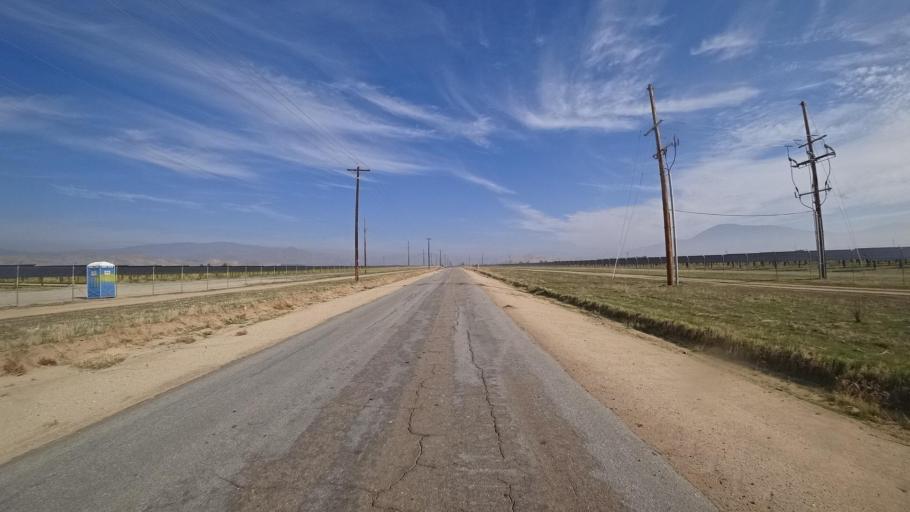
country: US
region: California
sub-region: Kern County
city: Arvin
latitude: 35.3257
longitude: -118.8147
